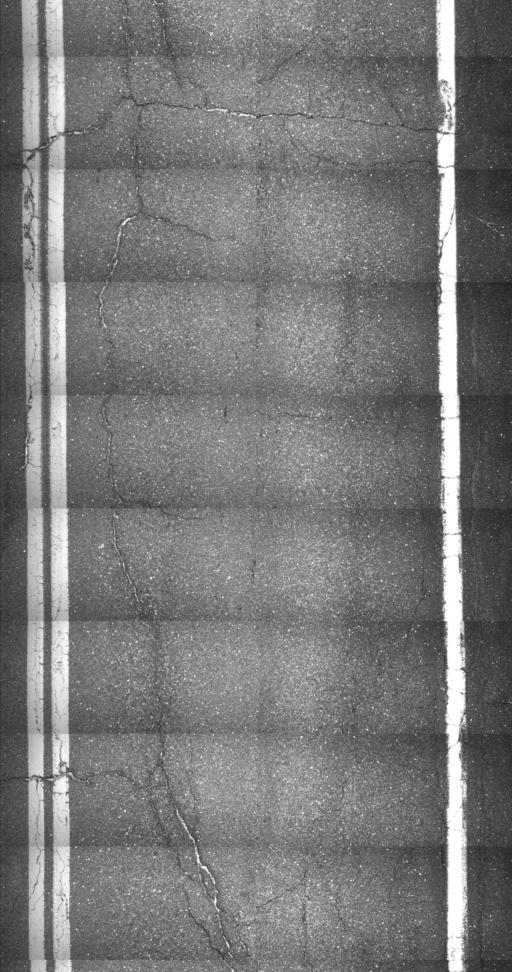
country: US
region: New Hampshire
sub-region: Sullivan County
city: Claremont
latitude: 43.3514
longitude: -72.4070
